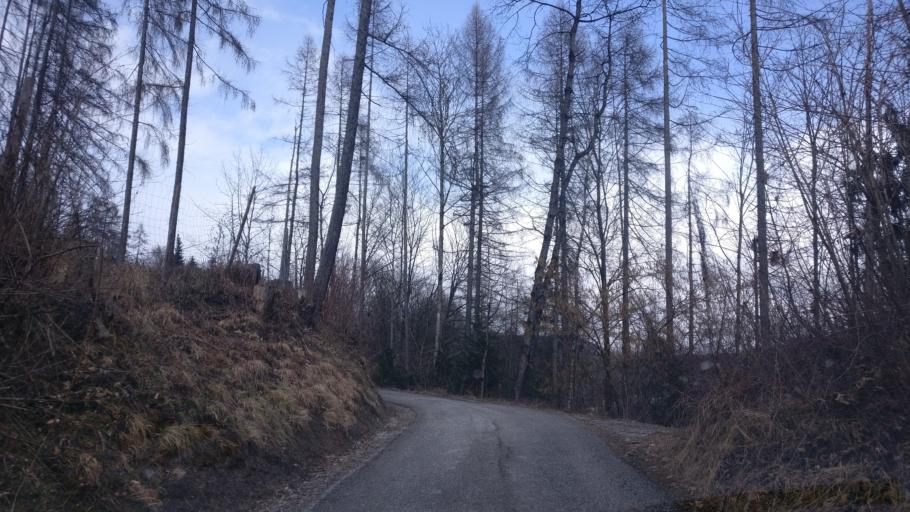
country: AT
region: Salzburg
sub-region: Politischer Bezirk Sankt Johann im Pongau
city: Bischofshofen
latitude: 47.4245
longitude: 13.2126
